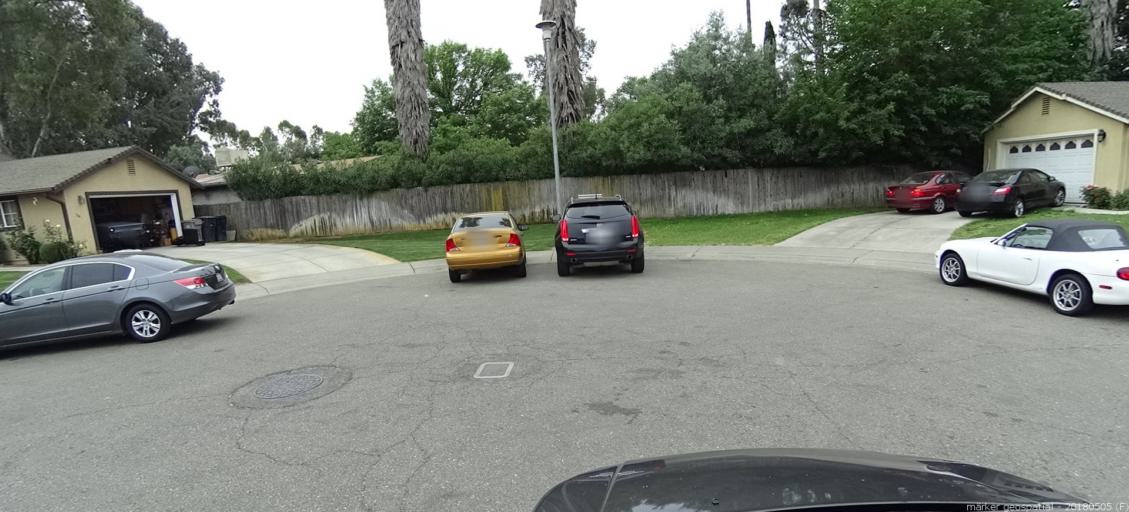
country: US
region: California
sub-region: Sacramento County
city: Rio Linda
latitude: 38.6595
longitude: -121.4433
